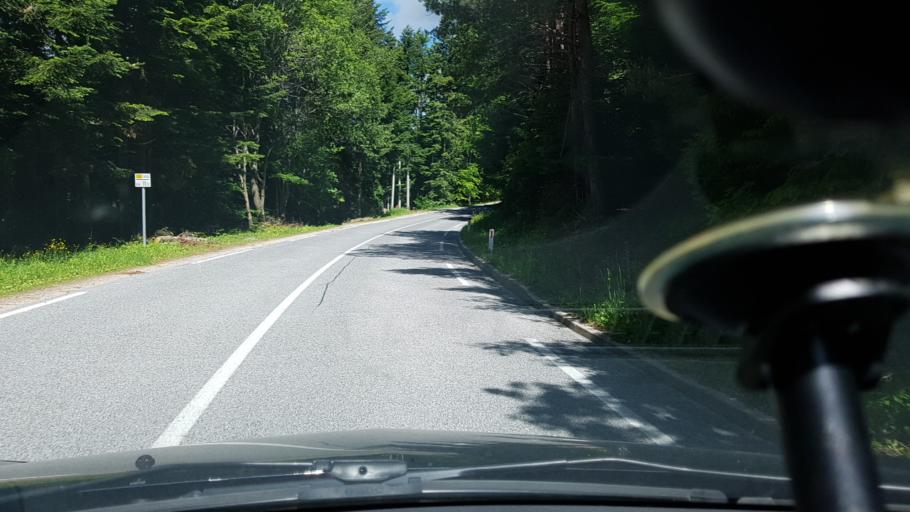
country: SI
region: Zrece
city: Zrece
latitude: 46.4242
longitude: 15.3711
